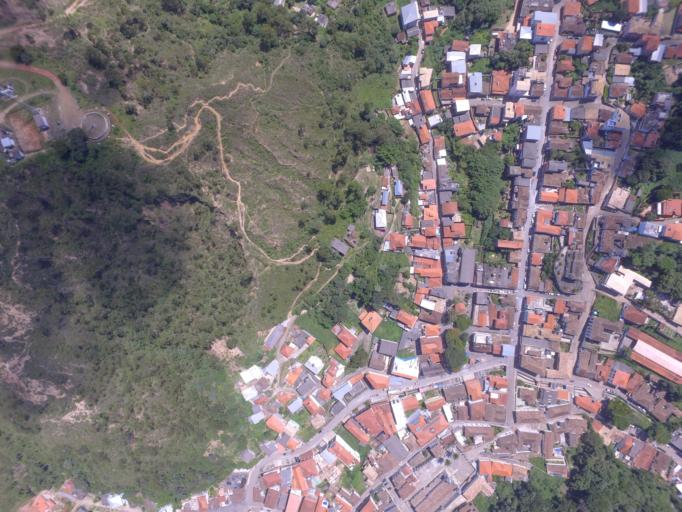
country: BR
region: Minas Gerais
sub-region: Tiradentes
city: Tiradentes
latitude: -21.0560
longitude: -44.0785
